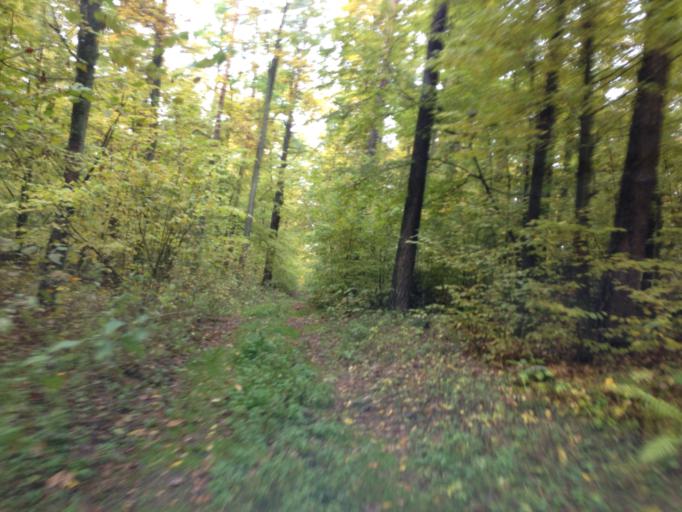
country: PL
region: Kujawsko-Pomorskie
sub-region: Powiat brodnicki
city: Gorzno
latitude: 53.2695
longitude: 19.7101
